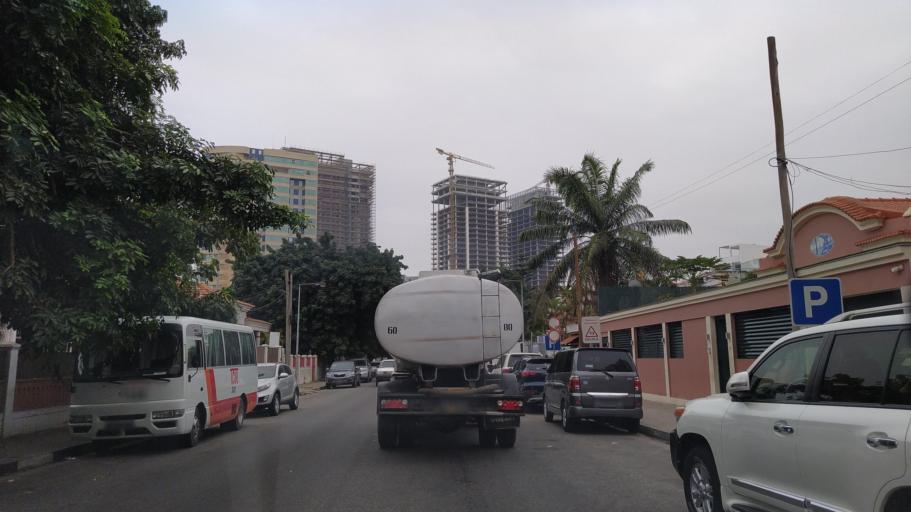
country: AO
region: Luanda
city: Luanda
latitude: -8.8192
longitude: 13.2369
